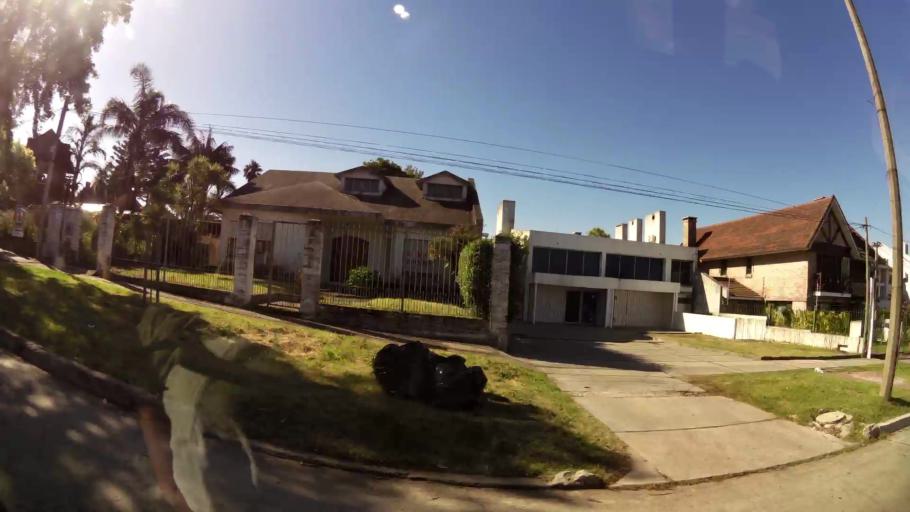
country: UY
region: Canelones
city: Paso de Carrasco
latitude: -34.8832
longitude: -56.0751
